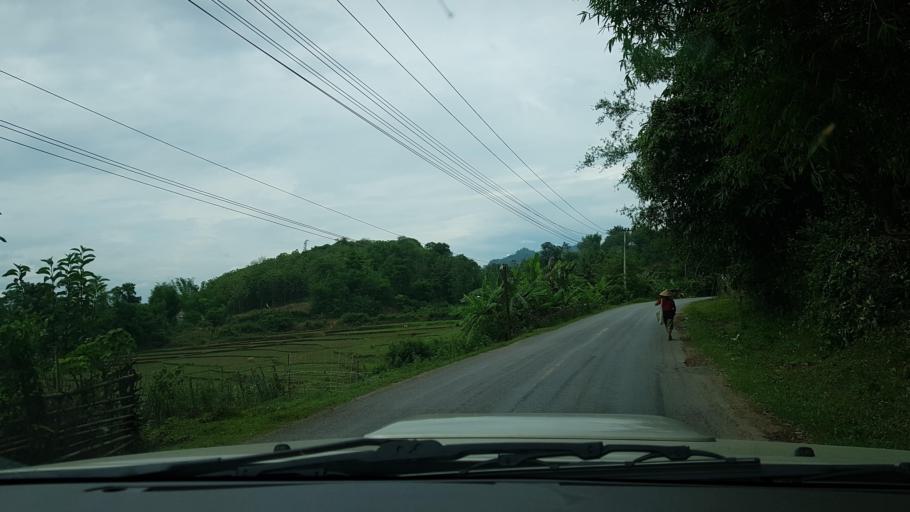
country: LA
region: Loungnamtha
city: Muang Nale
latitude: 20.3524
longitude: 101.6837
